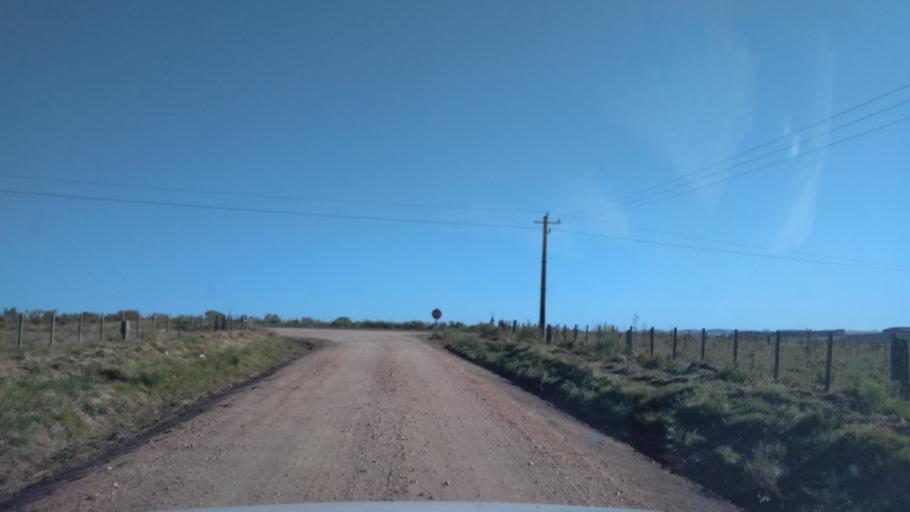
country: UY
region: Florida
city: Casupa
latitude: -34.0013
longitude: -55.7873
